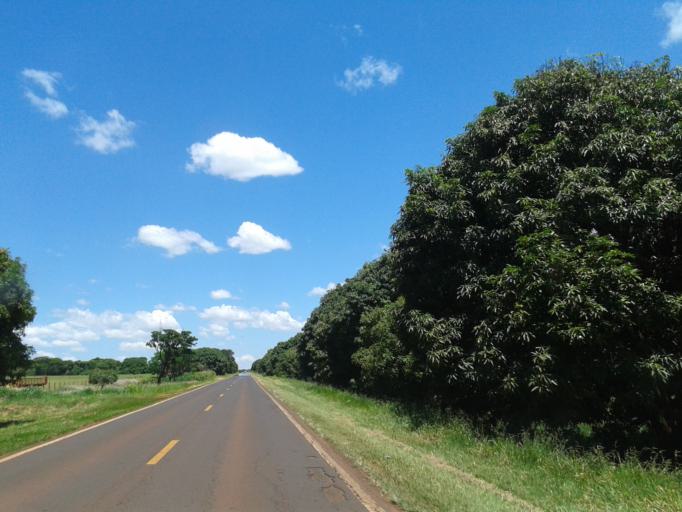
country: BR
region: Minas Gerais
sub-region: Centralina
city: Centralina
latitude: -18.7263
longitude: -49.1850
